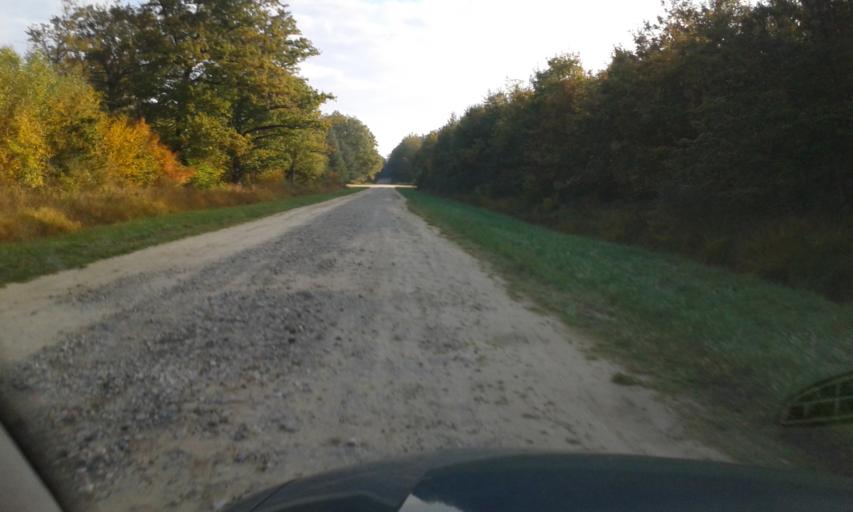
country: FR
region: Centre
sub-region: Departement du Loiret
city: Saran
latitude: 47.9744
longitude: 1.9014
